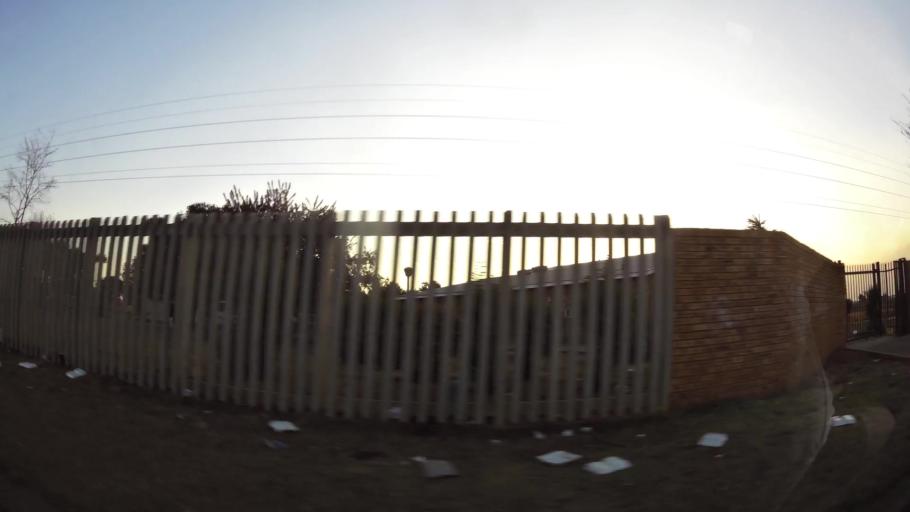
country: ZA
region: Gauteng
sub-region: West Rand District Municipality
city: Randfontein
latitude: -26.2007
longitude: 27.7081
